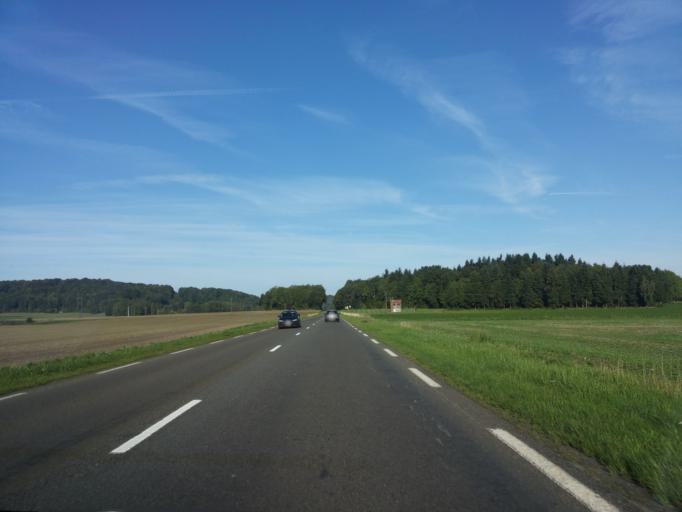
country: FR
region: Picardie
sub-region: Departement de l'Aisne
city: Crepy
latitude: 49.5936
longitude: 3.5368
